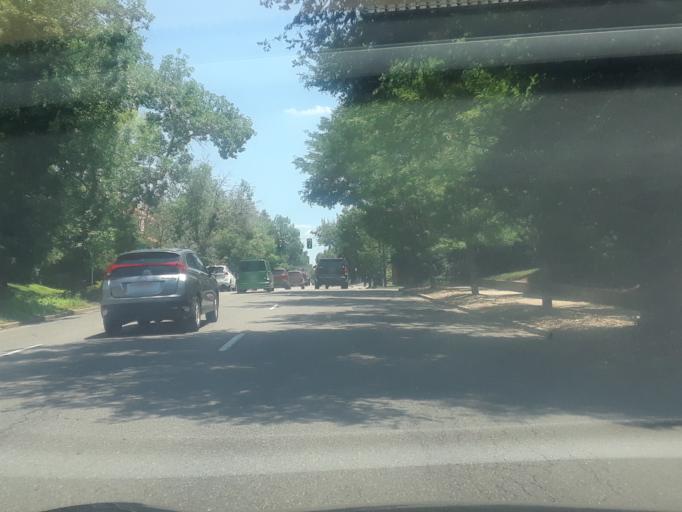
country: US
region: Colorado
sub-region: Denver County
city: Denver
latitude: 39.7255
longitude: -104.9690
